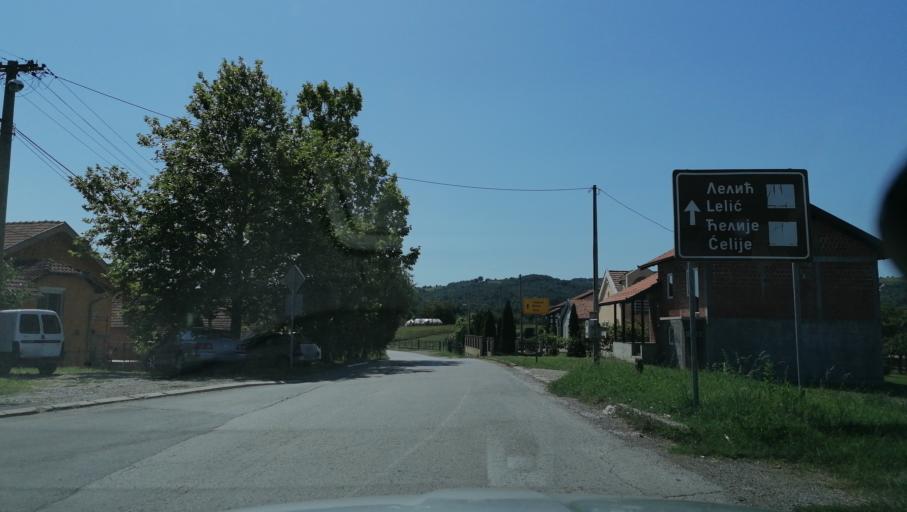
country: RS
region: Central Serbia
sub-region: Kolubarski Okrug
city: Valjevo
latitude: 44.2602
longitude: 19.8779
